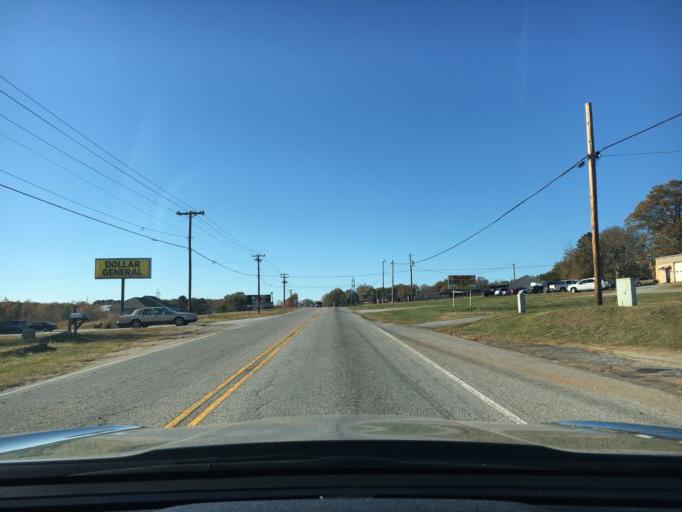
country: US
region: South Carolina
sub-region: Spartanburg County
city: Inman Mills
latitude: 35.0526
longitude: -82.1116
